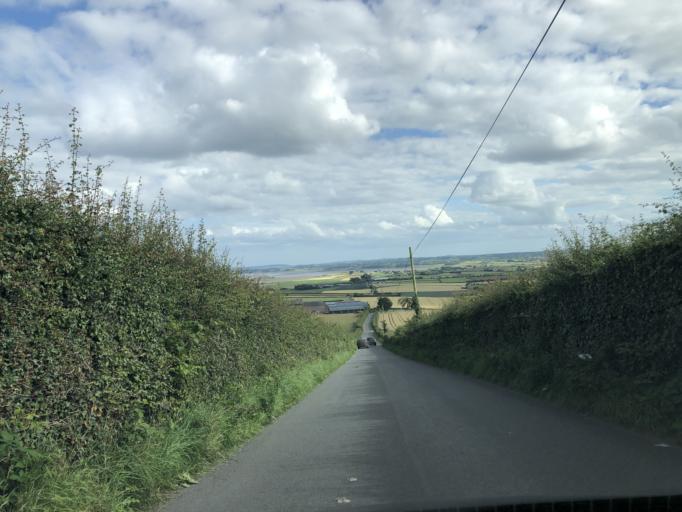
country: GB
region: Northern Ireland
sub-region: Ards District
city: Newtownards
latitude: 54.5765
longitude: -5.7175
